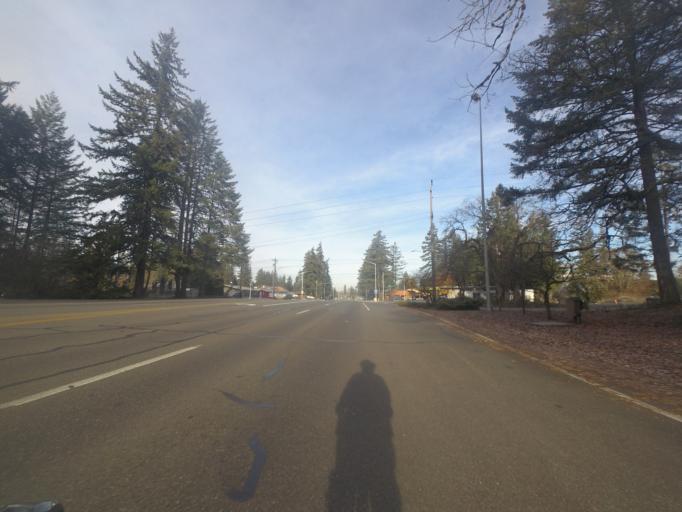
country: US
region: Washington
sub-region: Pierce County
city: McChord Air Force Base
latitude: 47.1389
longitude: -122.5016
